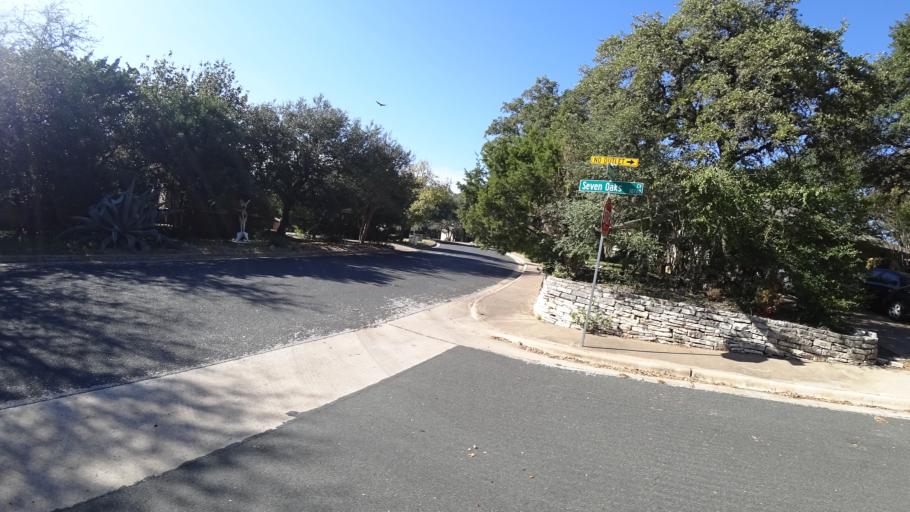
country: US
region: Texas
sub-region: Williamson County
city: Jollyville
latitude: 30.4160
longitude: -97.7707
